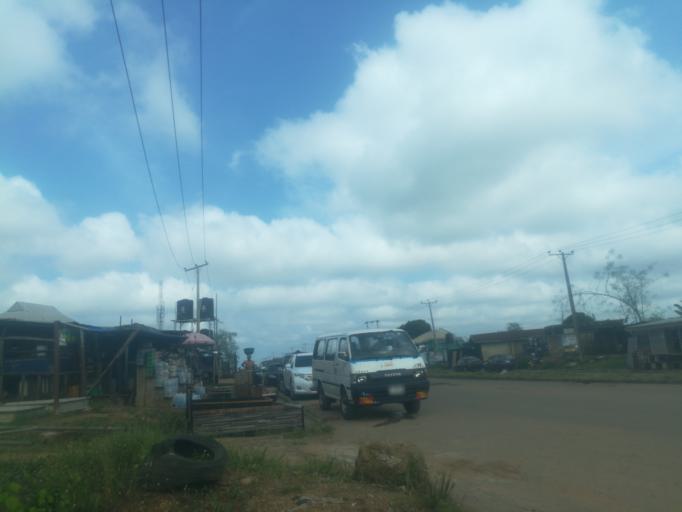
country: NG
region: Oyo
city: Ibadan
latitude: 7.3323
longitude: 3.8588
